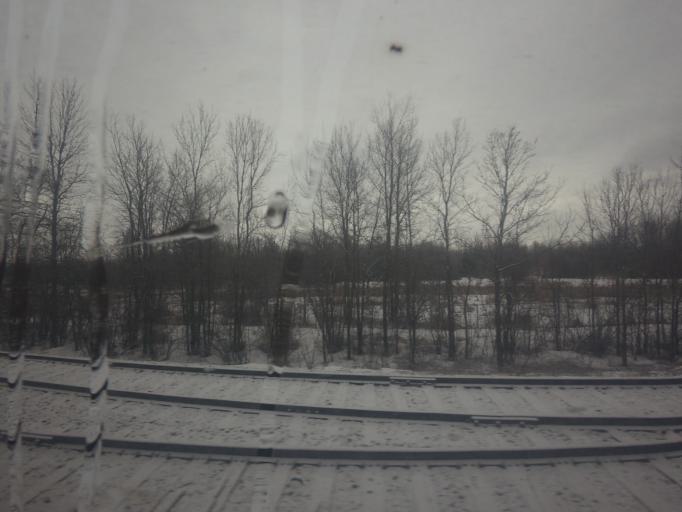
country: CA
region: Ontario
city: Bells Corners
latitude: 45.1852
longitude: -75.8242
